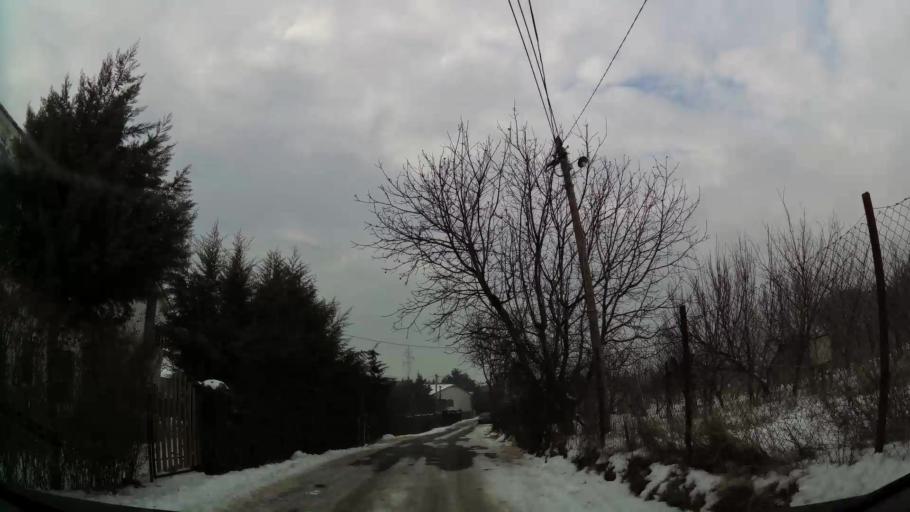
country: MK
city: Kondovo
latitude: 42.0374
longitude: 21.3437
